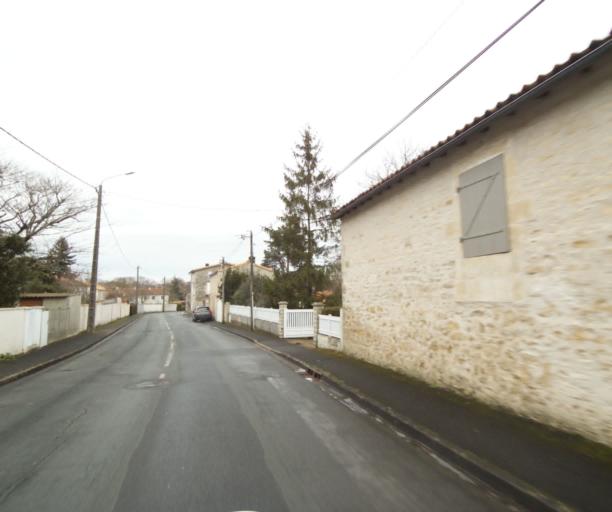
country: FR
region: Poitou-Charentes
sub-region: Departement des Deux-Sevres
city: Niort
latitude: 46.3397
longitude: -0.4542
